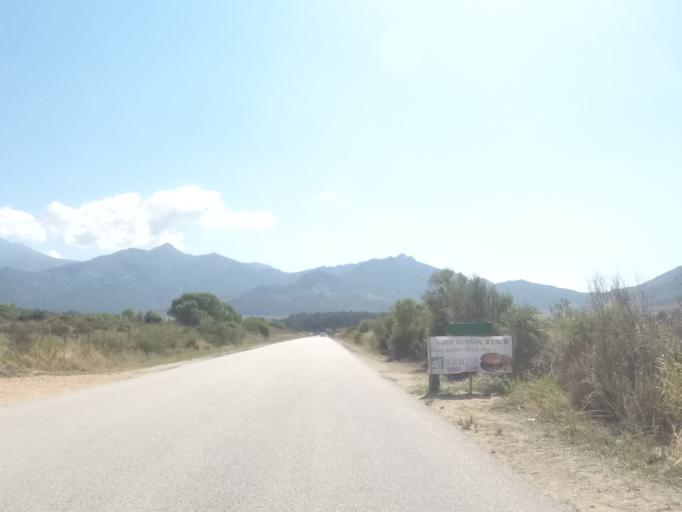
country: FR
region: Corsica
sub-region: Departement de la Haute-Corse
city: Calvi
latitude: 42.5115
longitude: 8.7911
